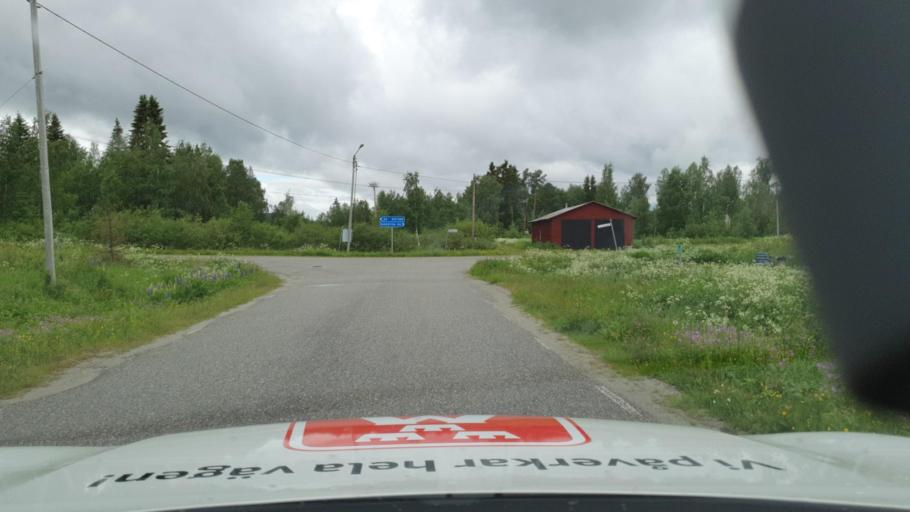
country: SE
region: Vaesterbotten
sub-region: Dorotea Kommun
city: Dorotea
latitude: 64.1034
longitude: 16.6413
